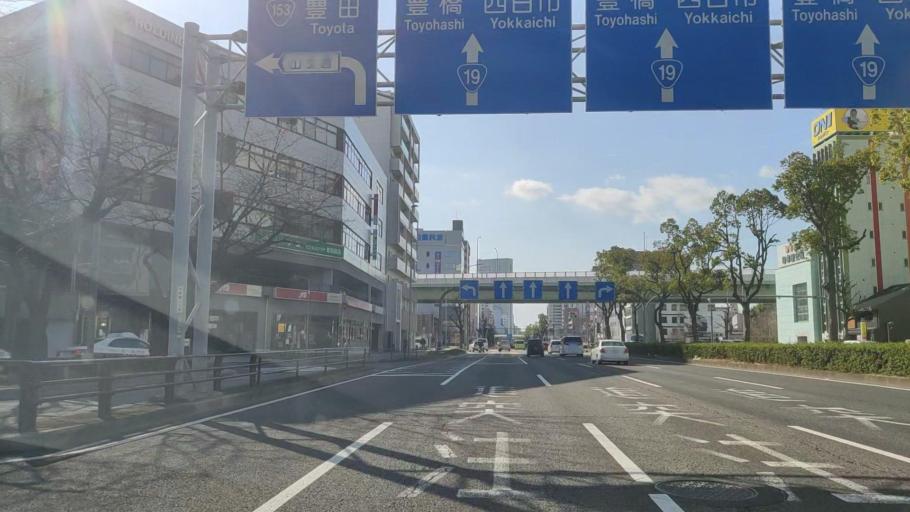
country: JP
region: Aichi
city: Nagoya-shi
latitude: 35.1526
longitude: 136.8990
